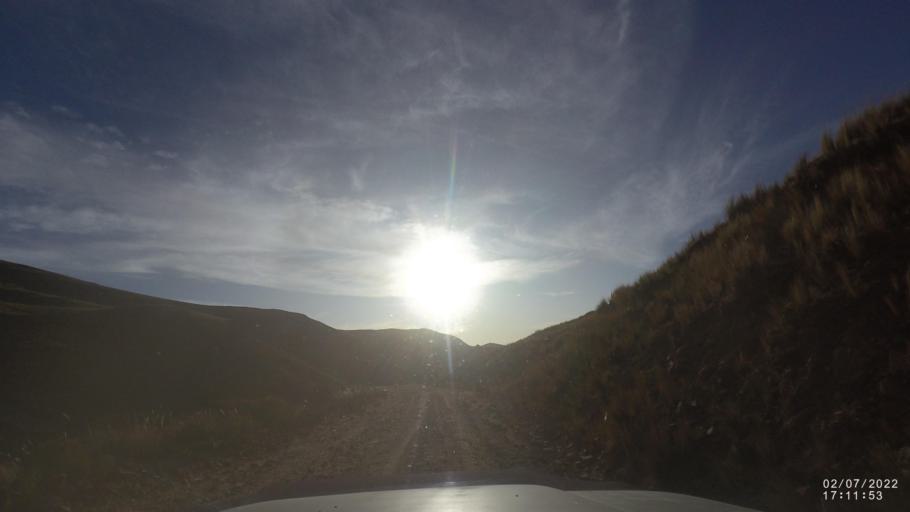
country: BO
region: Cochabamba
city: Irpa Irpa
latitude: -17.8878
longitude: -66.5671
